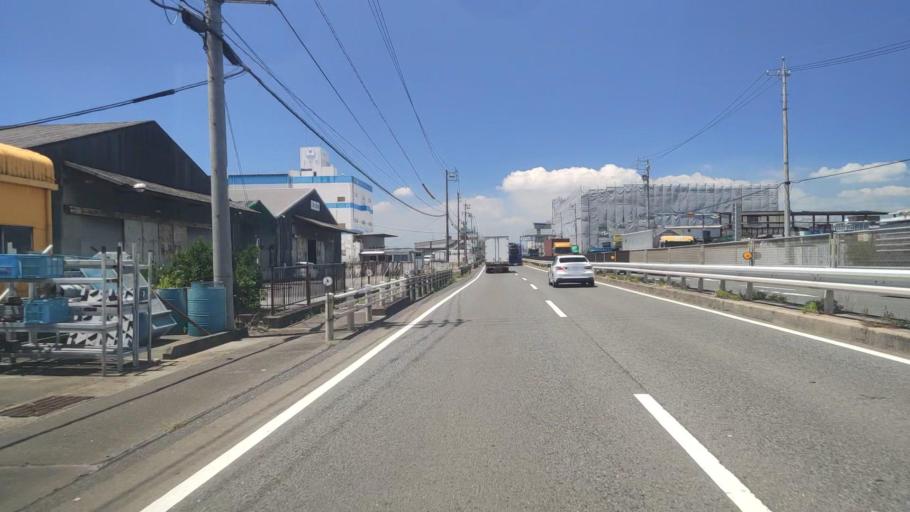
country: JP
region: Aichi
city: Kanie
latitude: 35.0771
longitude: 136.7950
